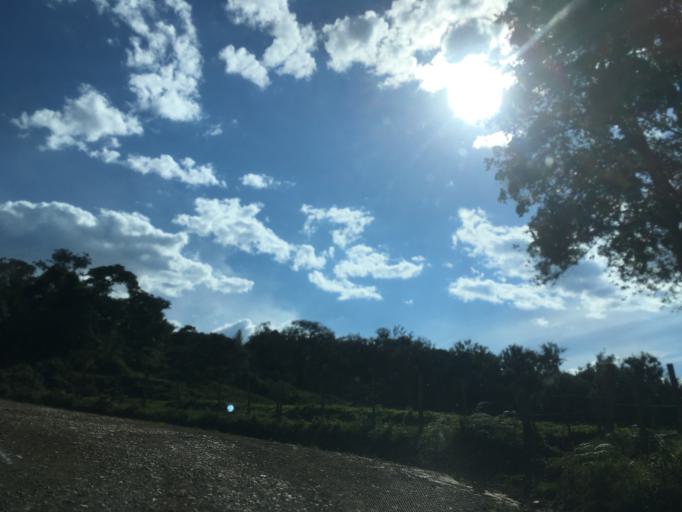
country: CO
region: Santander
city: Oiba
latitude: 6.1404
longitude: -73.1918
